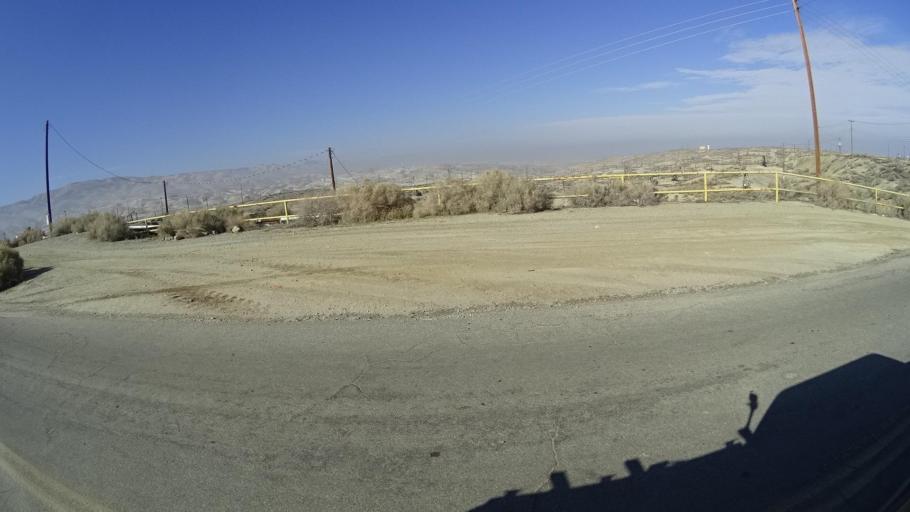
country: US
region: California
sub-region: Kern County
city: Taft Heights
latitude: 35.1189
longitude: -119.4781
